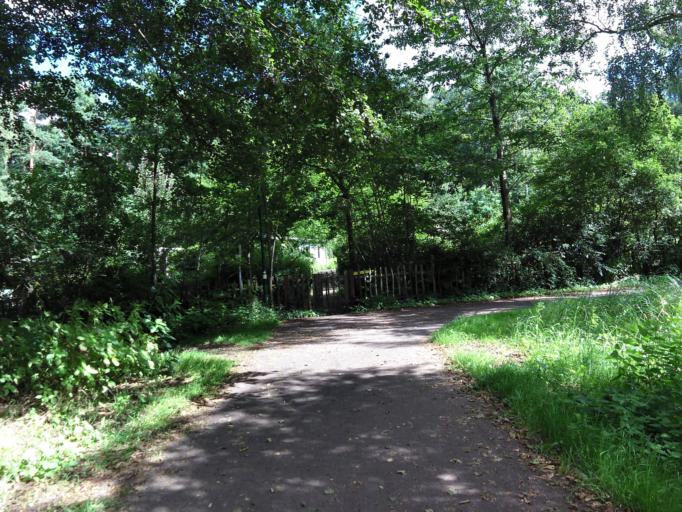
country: DE
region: Brandenburg
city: Lychen
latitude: 53.2154
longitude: 13.3026
